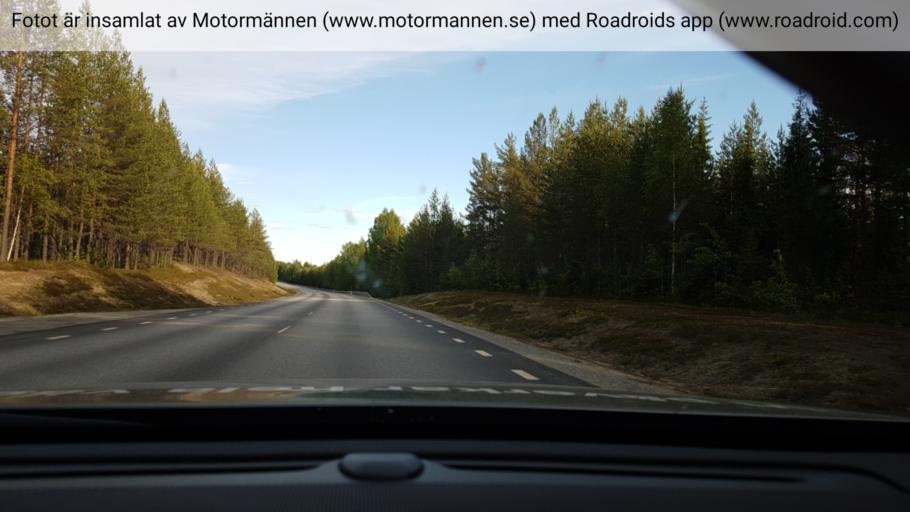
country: SE
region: Vaesterbotten
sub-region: Vindelns Kommun
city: Vindeln
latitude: 64.1517
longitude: 19.8563
